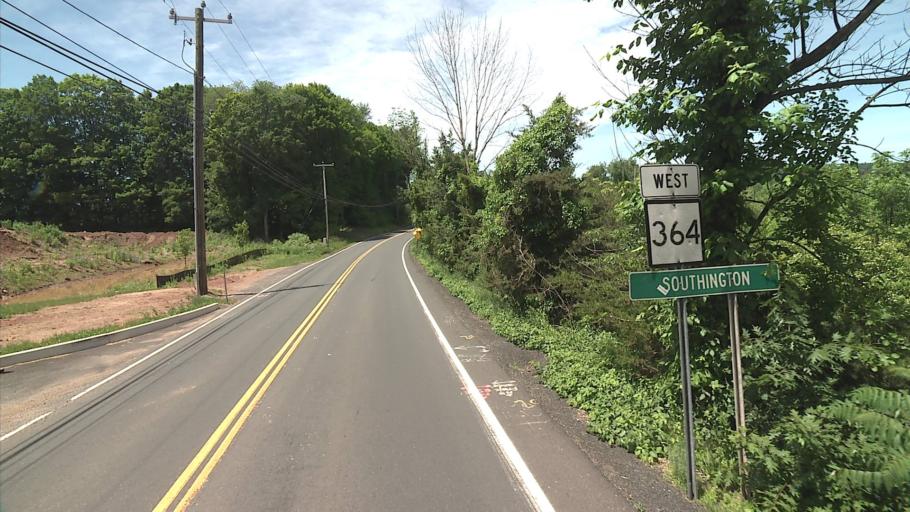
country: US
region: Connecticut
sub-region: Hartford County
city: Kensington
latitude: 41.6026
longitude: -72.7995
